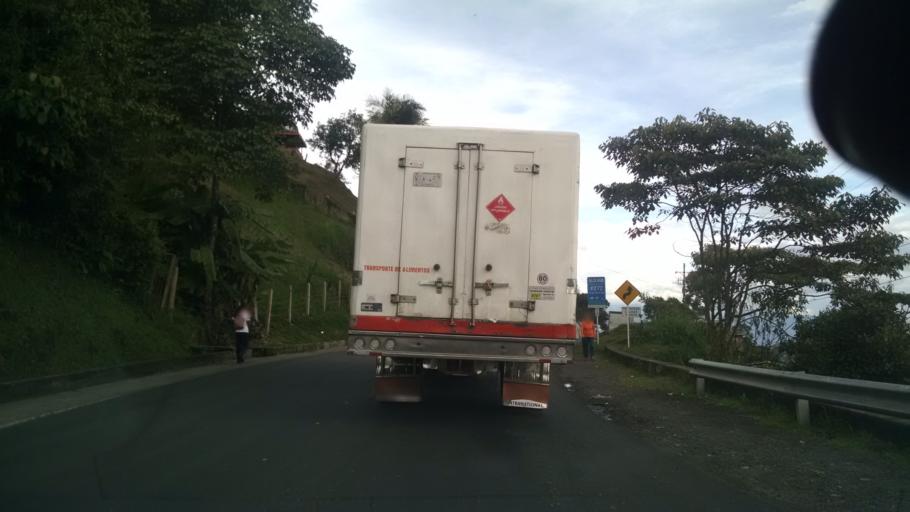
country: CO
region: Antioquia
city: Santa Barbara
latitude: 5.9166
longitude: -75.5788
